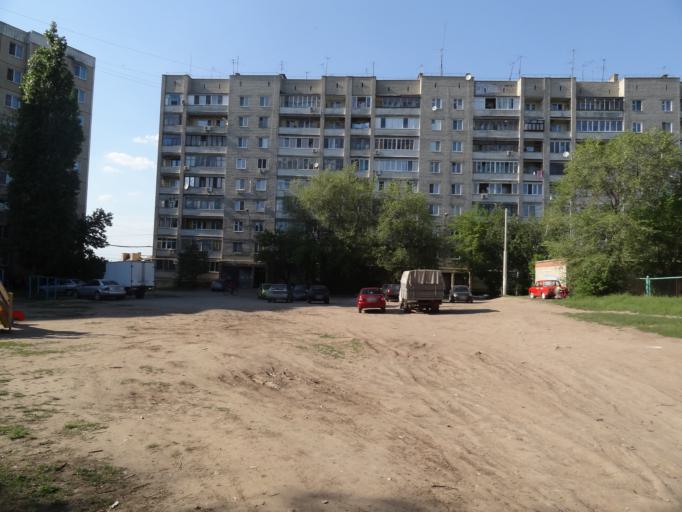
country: RU
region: Saratov
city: Privolzhskiy
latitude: 51.4112
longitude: 46.0433
